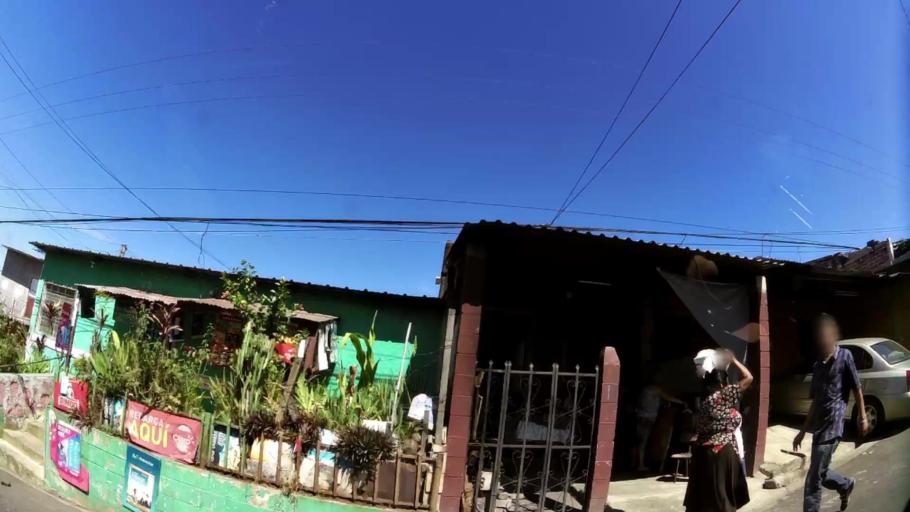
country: SV
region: Ahuachapan
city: Ahuachapan
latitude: 13.9291
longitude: -89.8406
